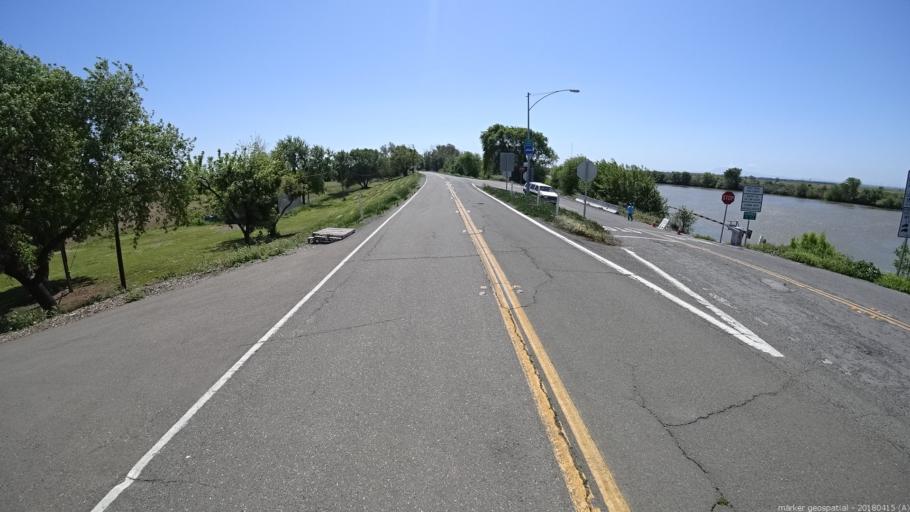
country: US
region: California
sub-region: Sacramento County
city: Walnut Grove
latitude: 38.2369
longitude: -121.6022
